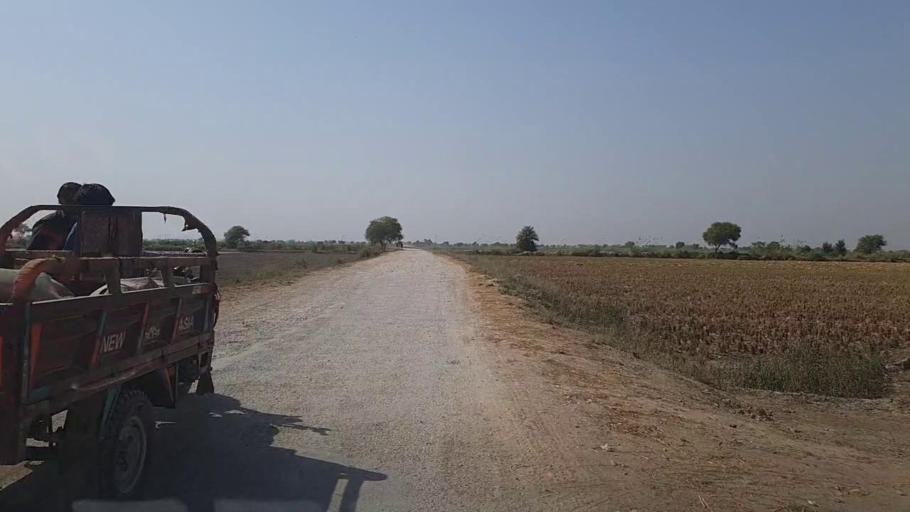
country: PK
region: Sindh
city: Kandhkot
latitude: 28.3933
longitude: 69.3134
